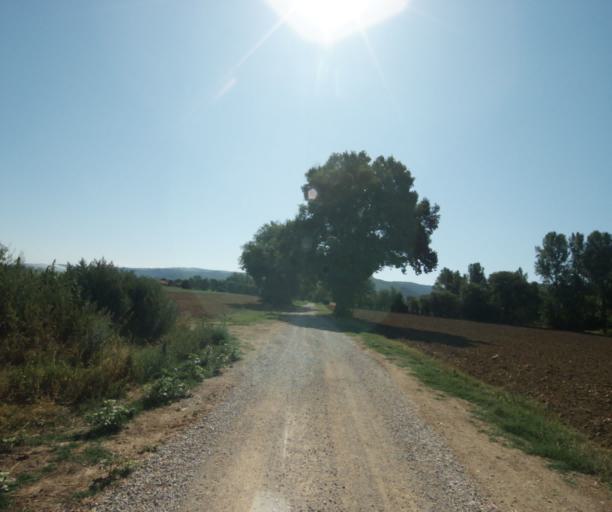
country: FR
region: Midi-Pyrenees
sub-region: Departement de la Haute-Garonne
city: Revel
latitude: 43.4611
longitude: 2.0347
